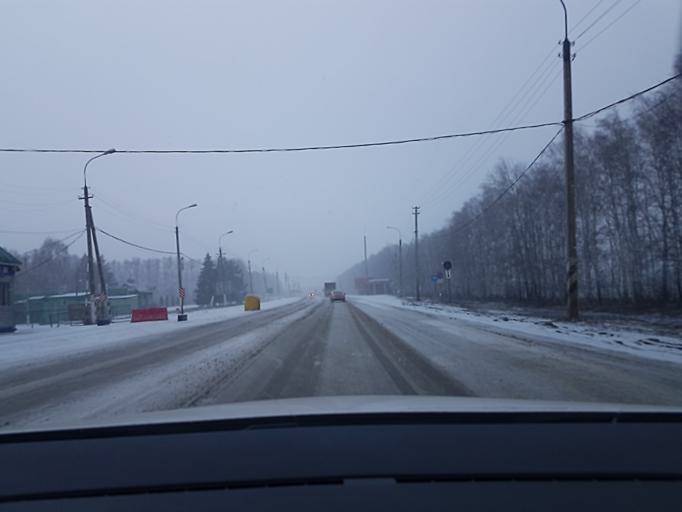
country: RU
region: Tambov
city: Pervomayskiy
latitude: 53.3119
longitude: 40.2202
